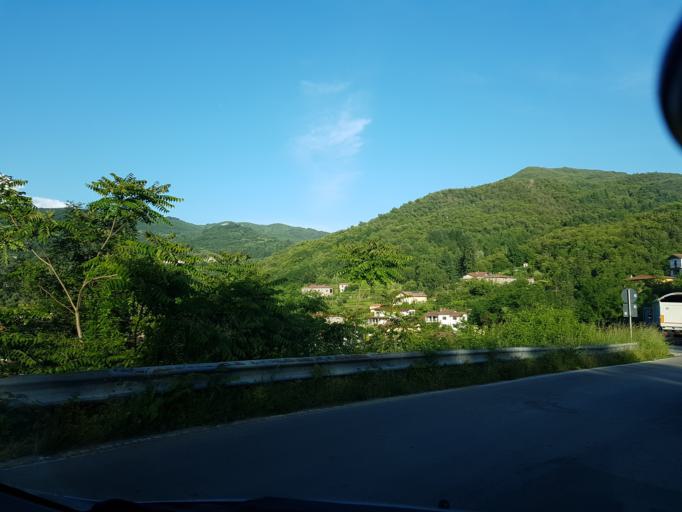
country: IT
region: Tuscany
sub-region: Provincia di Massa-Carrara
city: Casola in Lunigiana
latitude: 44.1925
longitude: 10.1950
